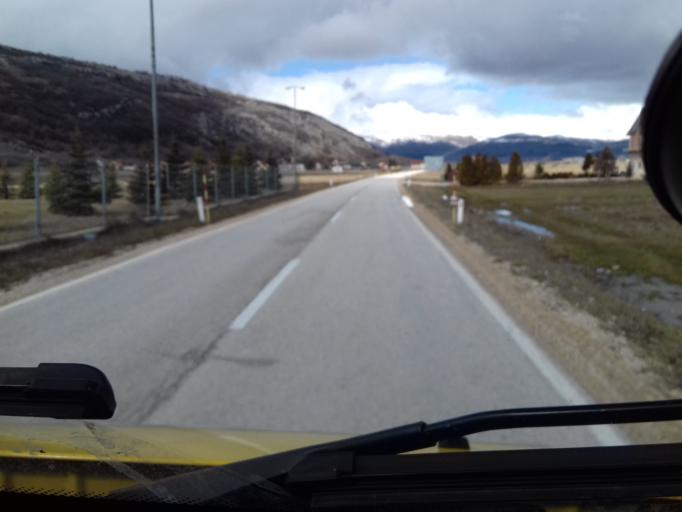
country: BA
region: Federation of Bosnia and Herzegovina
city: Tomislavgrad
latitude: 43.6534
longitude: 17.2190
